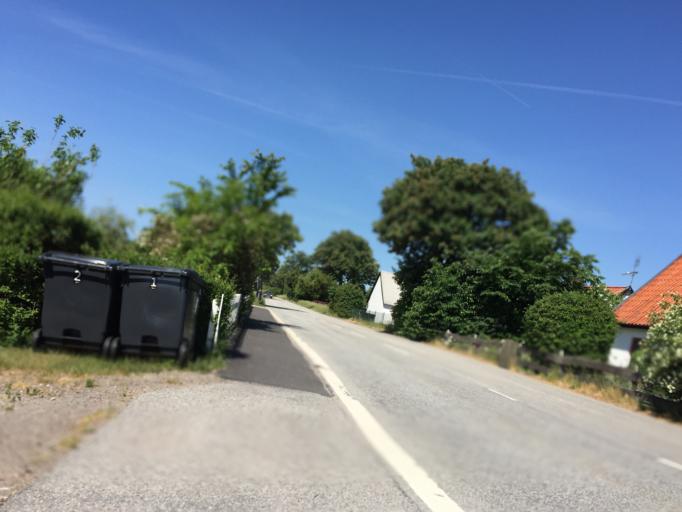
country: SE
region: Skane
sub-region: Trelleborgs Kommun
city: Trelleborg
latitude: 55.3541
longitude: 13.2492
